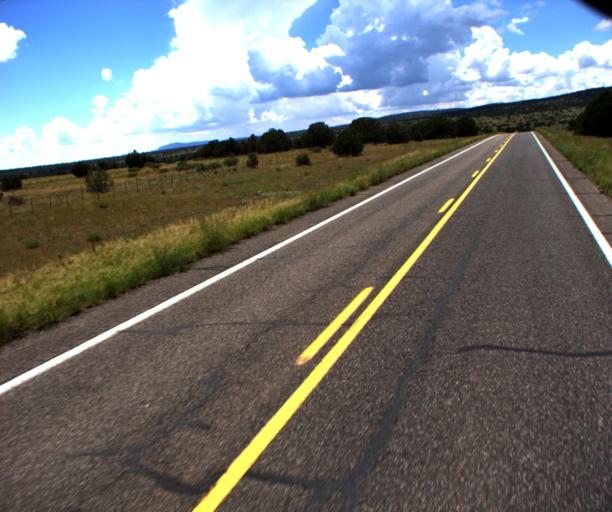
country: US
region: Arizona
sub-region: Gila County
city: Pine
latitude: 34.5059
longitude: -111.5704
